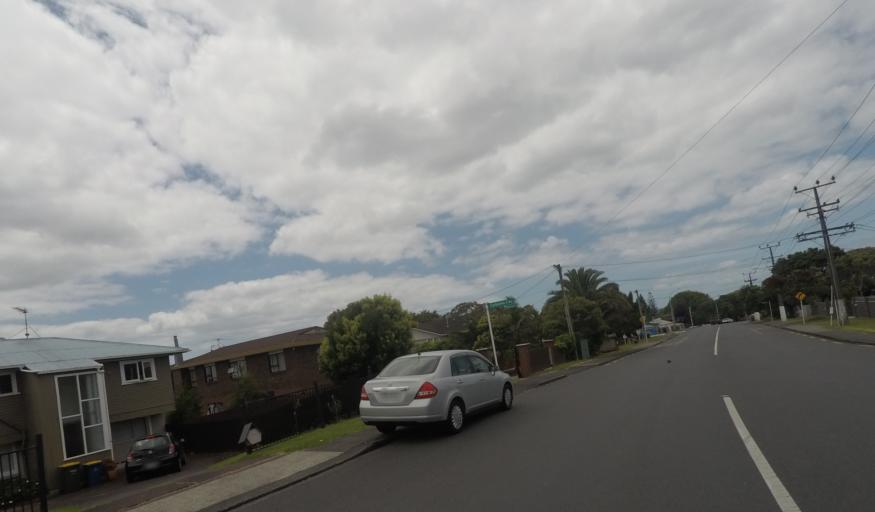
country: NZ
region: Auckland
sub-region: Auckland
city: Rosebank
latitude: -36.8306
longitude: 174.6086
